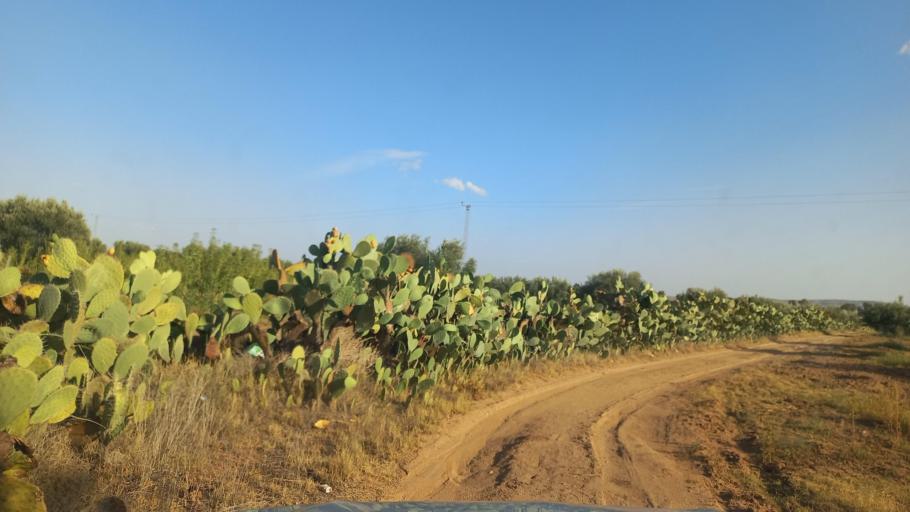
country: TN
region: Al Qasrayn
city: Kasserine
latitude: 35.2678
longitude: 9.0326
